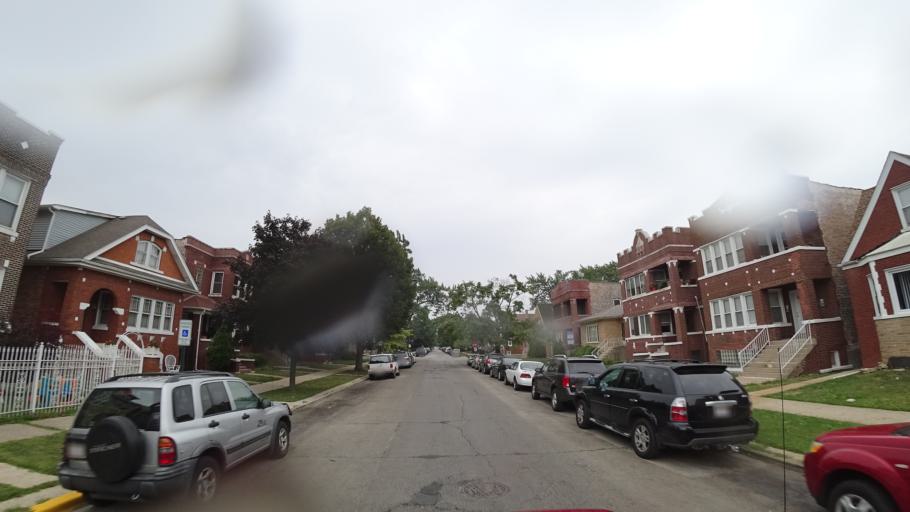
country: US
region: Illinois
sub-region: Cook County
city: Cicero
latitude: 41.8574
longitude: -87.7469
